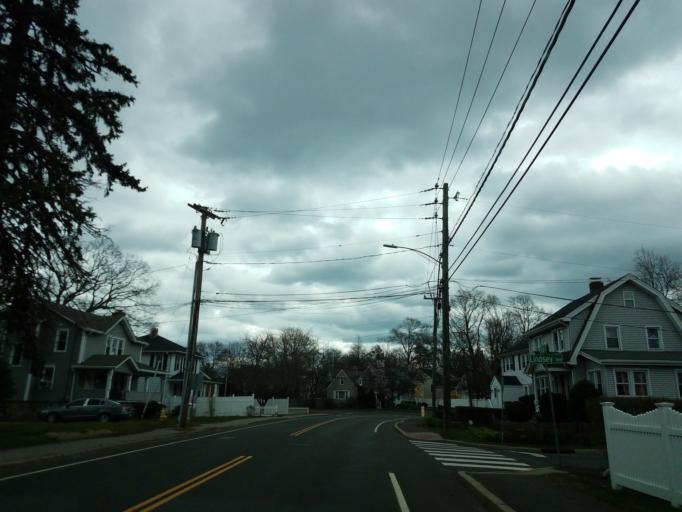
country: US
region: Connecticut
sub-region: Fairfield County
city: Stamford
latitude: 41.0786
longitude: -73.5360
